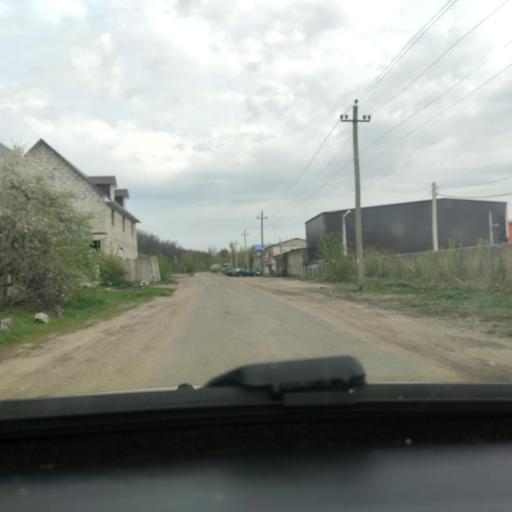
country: RU
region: Voronezj
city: Pridonskoy
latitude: 51.7334
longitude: 39.0606
